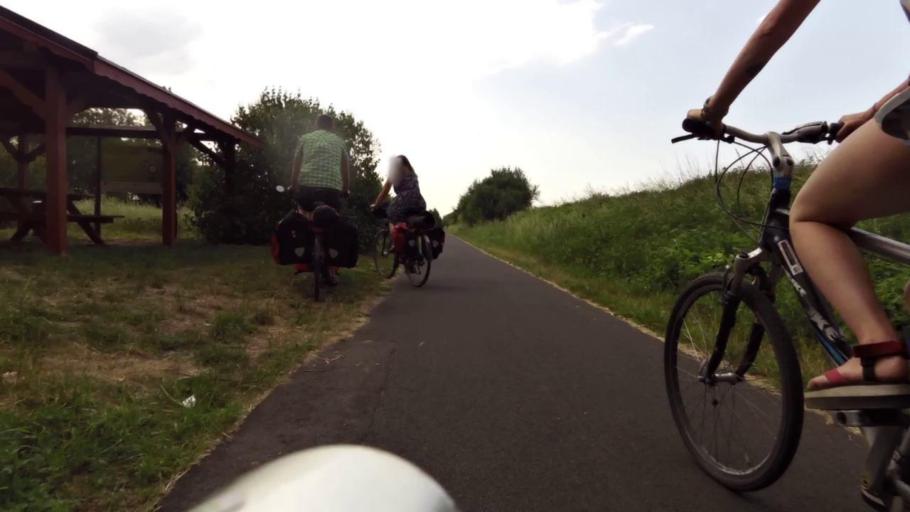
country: PL
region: Kujawsko-Pomorskie
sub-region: Powiat torunski
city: Lubianka
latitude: 53.1344
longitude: 18.4622
